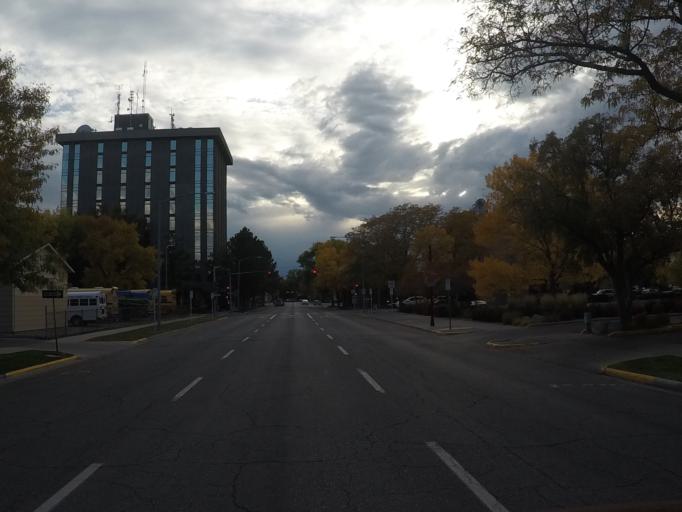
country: US
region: Montana
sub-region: Yellowstone County
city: Billings
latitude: 45.7819
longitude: -108.5115
